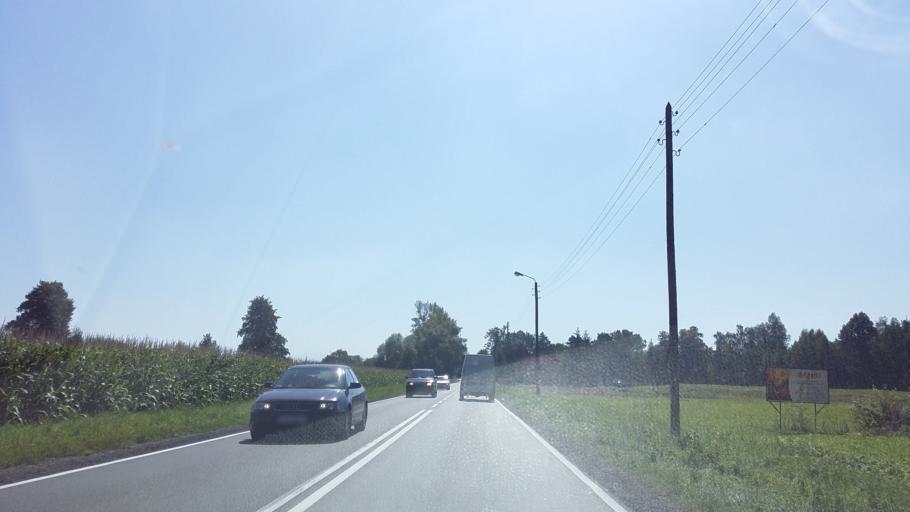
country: PL
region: Lesser Poland Voivodeship
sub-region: Powiat oswiecimski
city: Zator
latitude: 49.9819
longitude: 19.4384
